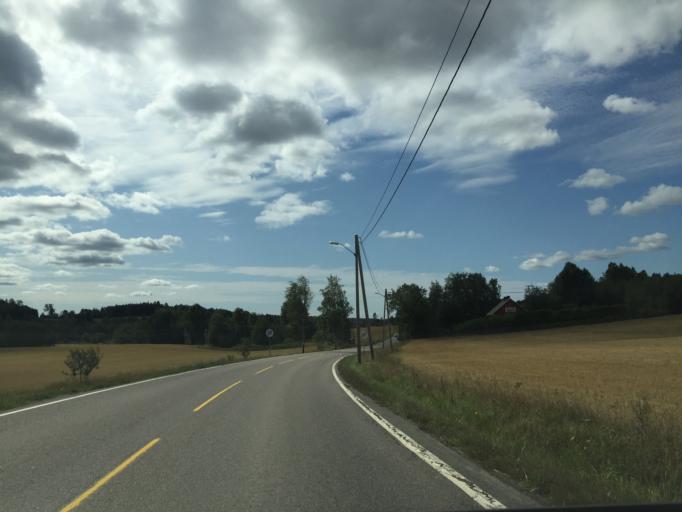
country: NO
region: Ostfold
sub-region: Hobol
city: Elvestad
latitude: 59.6199
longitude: 10.9460
